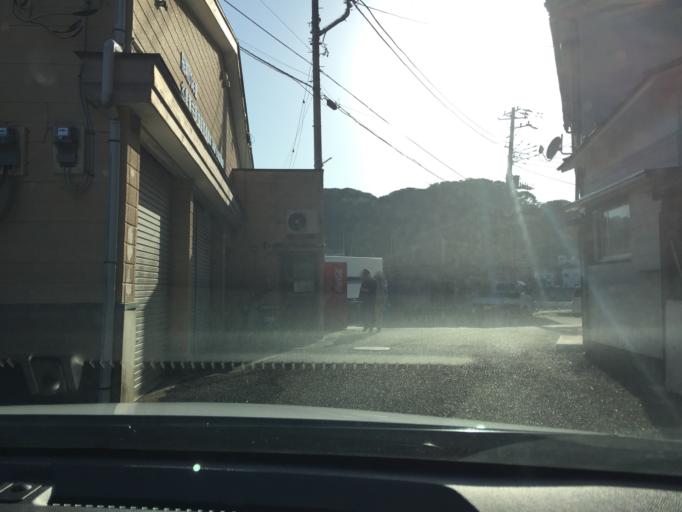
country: JP
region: Shizuoka
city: Shimoda
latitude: 34.6559
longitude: 138.9689
